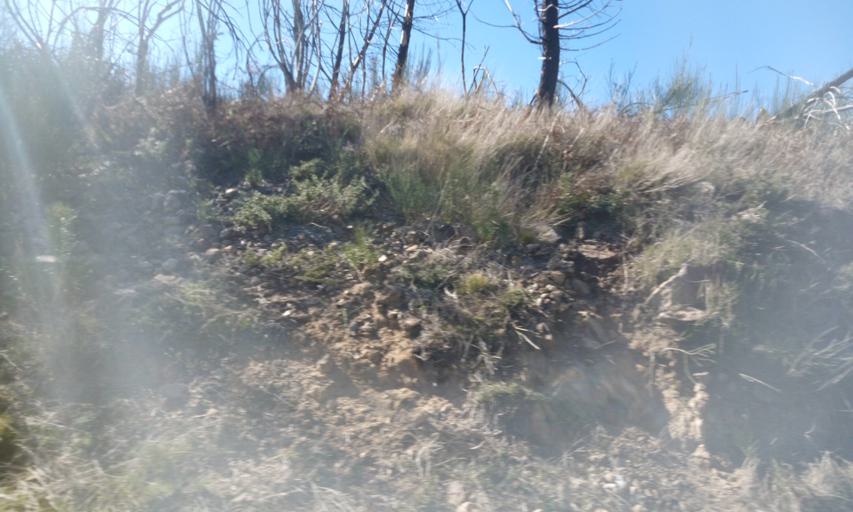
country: PT
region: Guarda
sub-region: Manteigas
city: Manteigas
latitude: 40.4940
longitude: -7.5423
